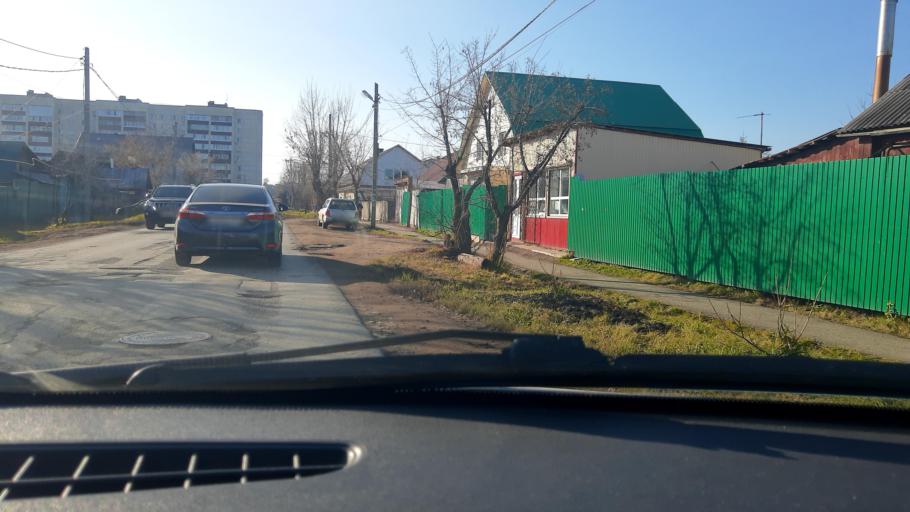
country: RU
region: Bashkortostan
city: Avdon
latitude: 54.6997
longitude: 55.8206
